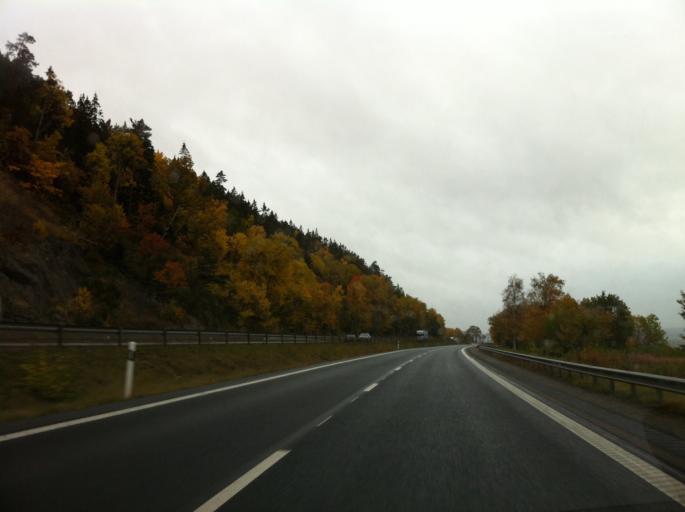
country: SE
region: Joenkoeping
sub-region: Jonkopings Kommun
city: Kaxholmen
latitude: 57.8921
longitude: 14.2894
